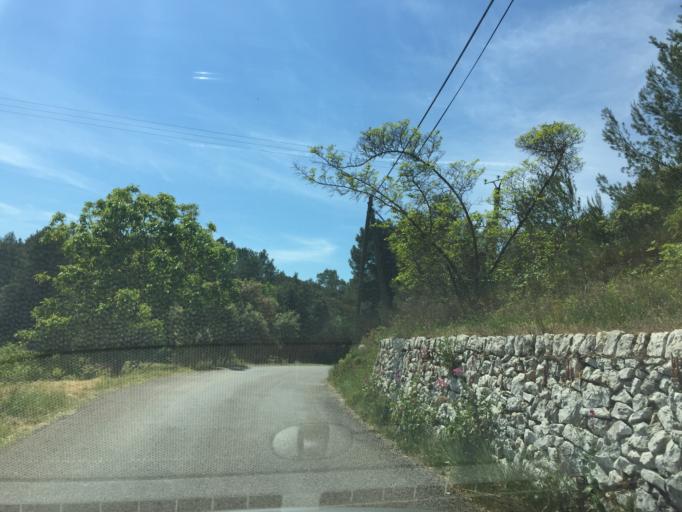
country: FR
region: Provence-Alpes-Cote d'Azur
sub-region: Departement du Var
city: Lorgues
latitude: 43.4778
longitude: 6.3680
